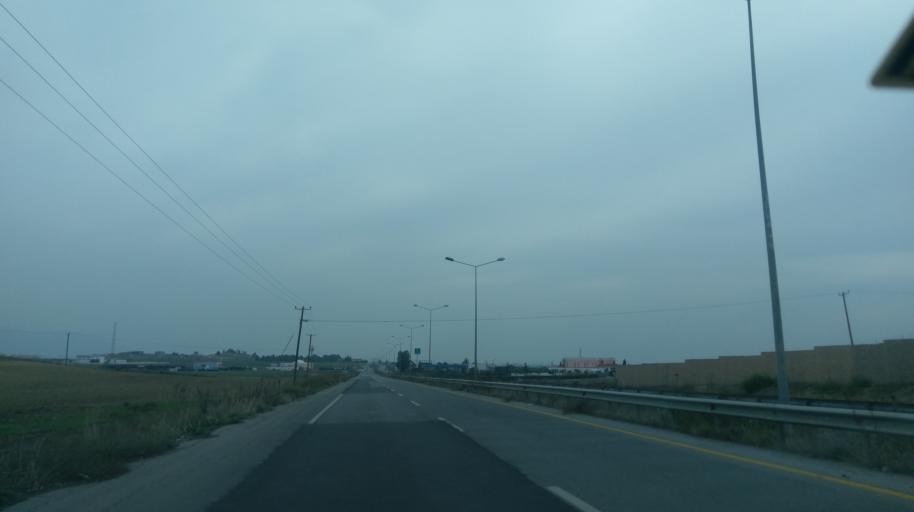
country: CY
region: Lefkosia
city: Mammari
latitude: 35.2117
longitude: 33.2390
